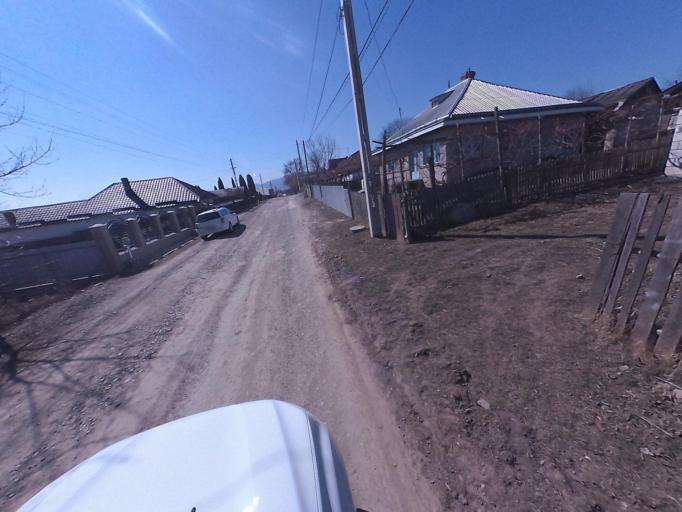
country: RO
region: Neamt
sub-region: Oras Targu Neamt
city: Humulesti
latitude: 47.1881
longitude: 26.3357
